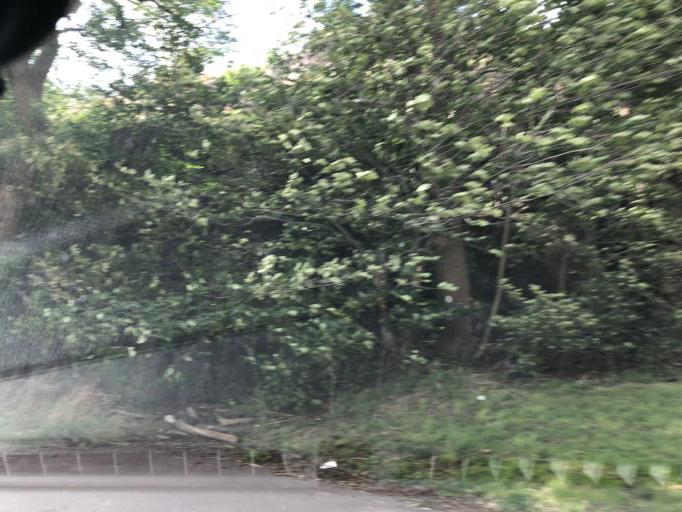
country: SE
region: Vaestra Goetaland
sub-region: Goteborg
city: Goeteborg
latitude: 57.7287
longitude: 11.9645
